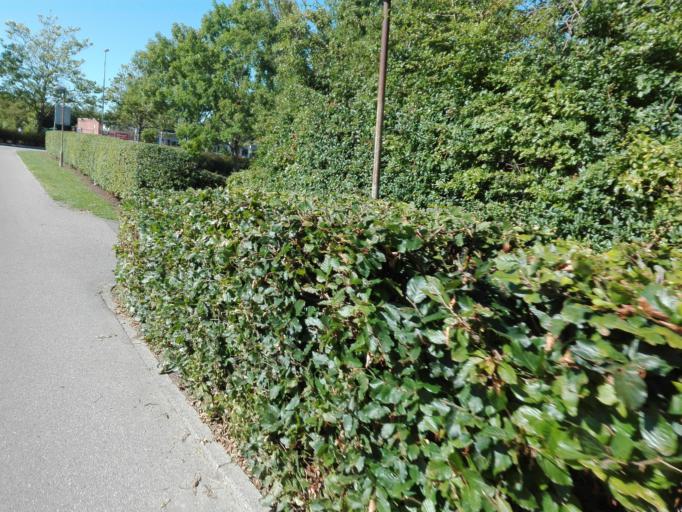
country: DK
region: Central Jutland
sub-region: Arhus Kommune
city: Stavtrup
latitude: 56.1121
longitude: 10.1517
